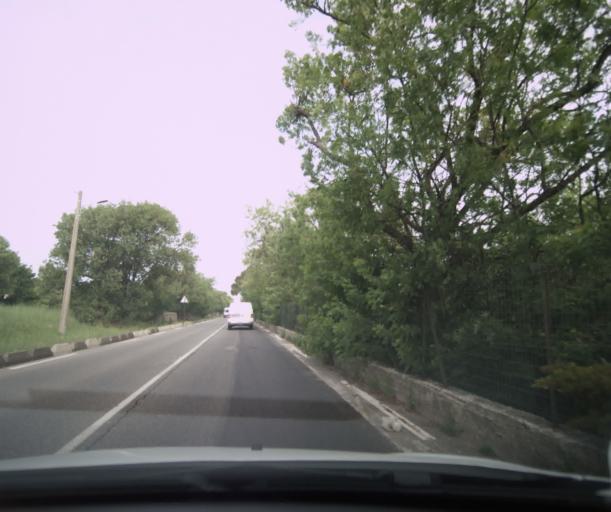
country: FR
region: Provence-Alpes-Cote d'Azur
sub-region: Departement du Var
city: Le Pradet
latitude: 43.1103
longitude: 6.0208
